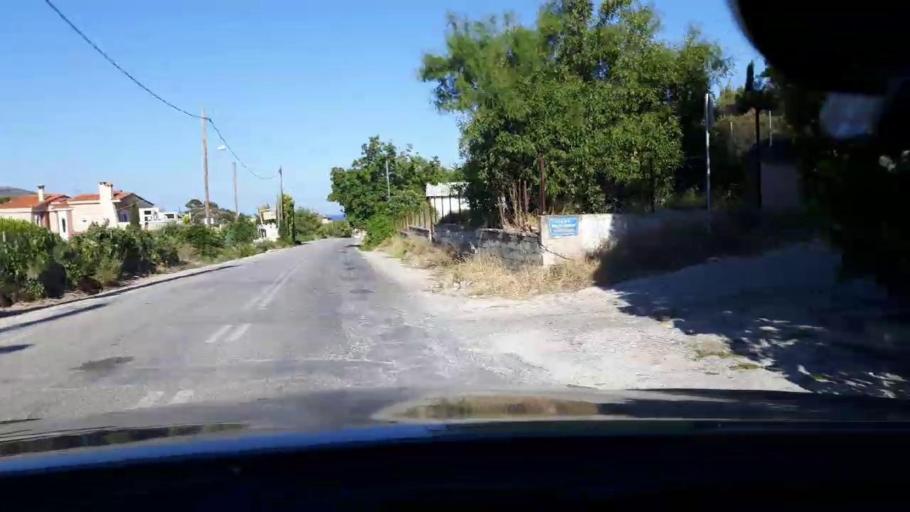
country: GR
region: Attica
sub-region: Nomarchia Anatolikis Attikis
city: Limin Mesoyaias
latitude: 37.8883
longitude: 23.9893
